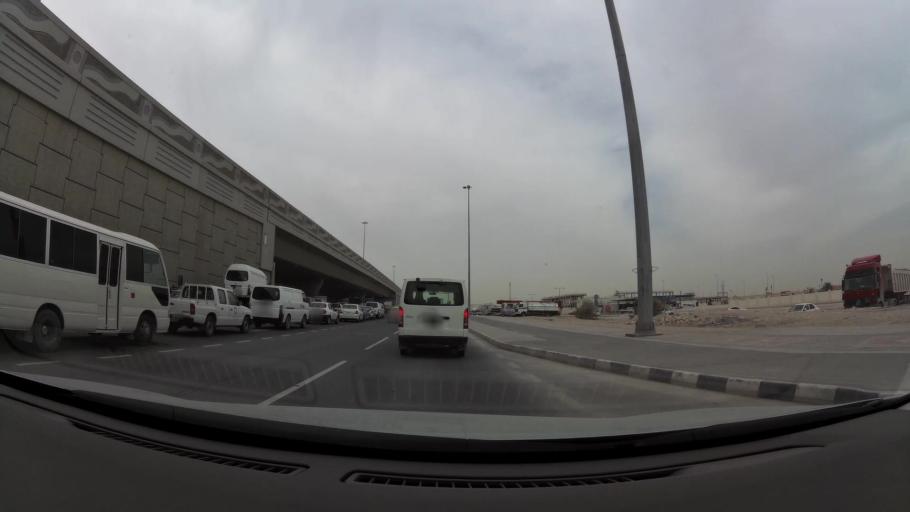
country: QA
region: Baladiyat ar Rayyan
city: Ar Rayyan
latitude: 25.2134
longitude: 51.4409
